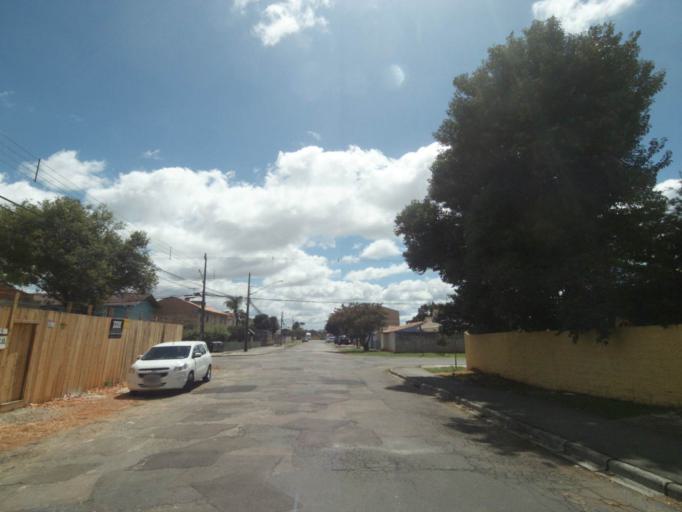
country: BR
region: Parana
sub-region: Pinhais
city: Pinhais
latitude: -25.4414
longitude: -49.2054
